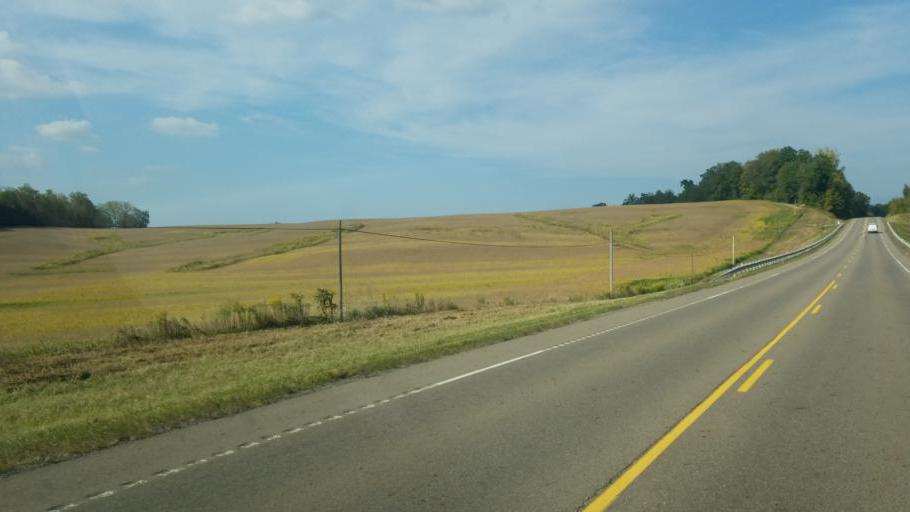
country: US
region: Ohio
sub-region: Licking County
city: Utica
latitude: 40.2562
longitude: -82.4064
